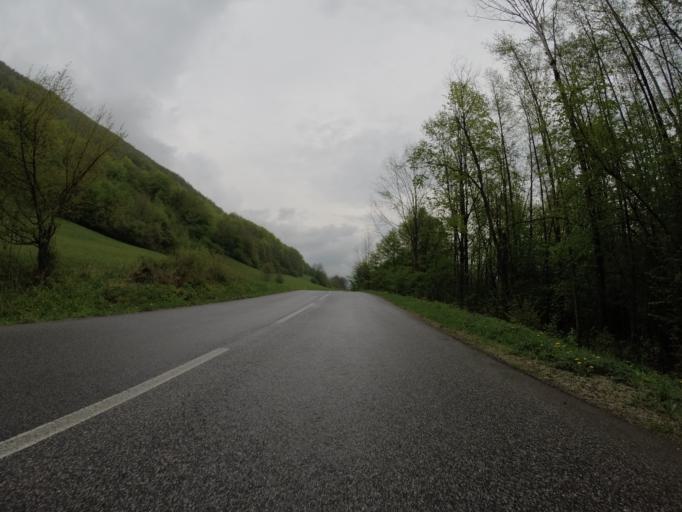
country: SK
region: Banskobystricky
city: Tisovec
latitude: 48.7243
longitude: 20.0139
